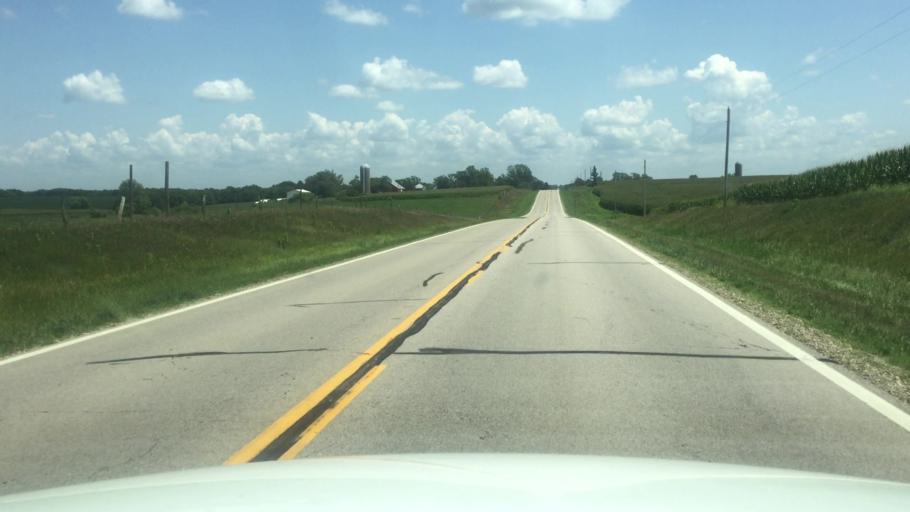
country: US
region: Kansas
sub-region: Brown County
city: Horton
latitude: 39.6674
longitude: -95.5909
